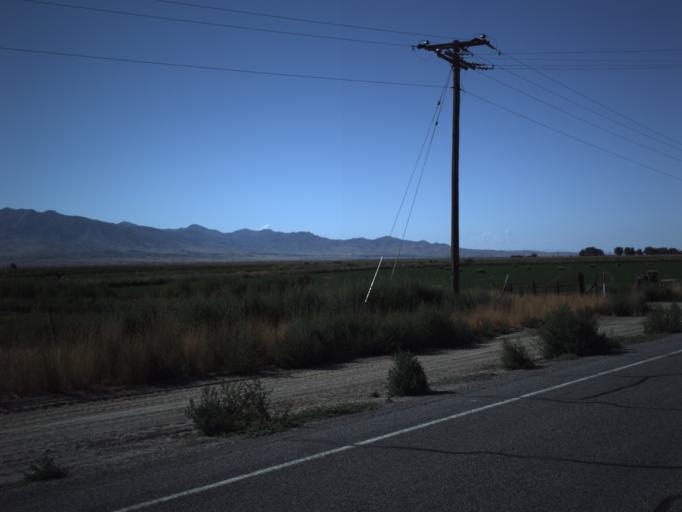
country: US
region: Utah
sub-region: Millard County
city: Delta
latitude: 39.5388
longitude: -112.3642
